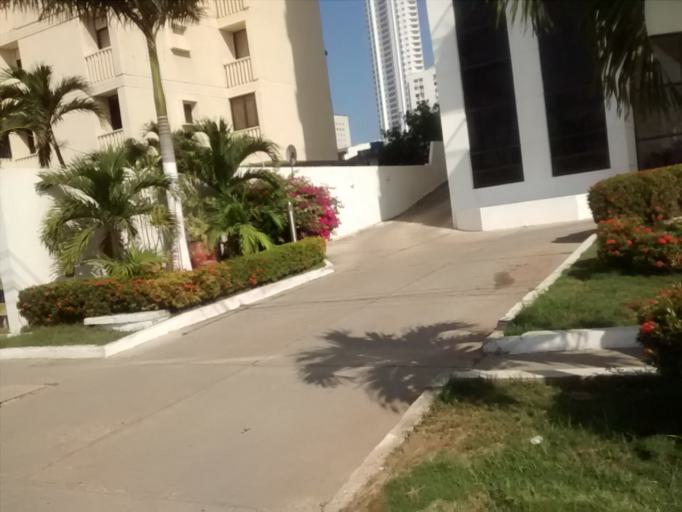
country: CO
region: Bolivar
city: Cartagena
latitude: 10.4017
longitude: -75.5530
